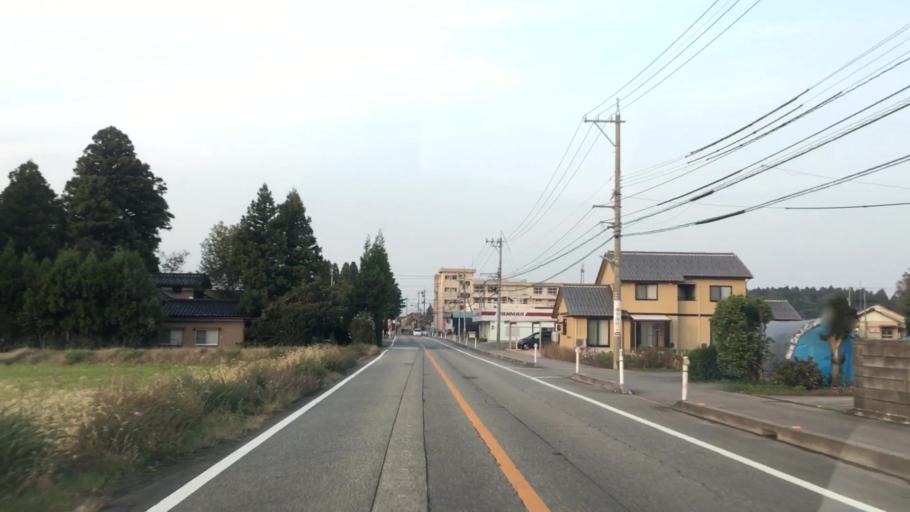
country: JP
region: Toyama
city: Toyama-shi
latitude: 36.6202
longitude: 137.2517
